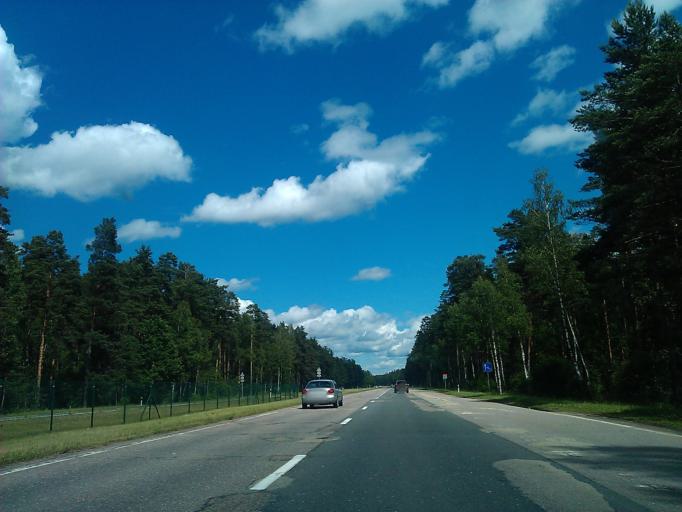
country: LV
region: Garkalne
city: Garkalne
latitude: 57.0427
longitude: 24.4250
